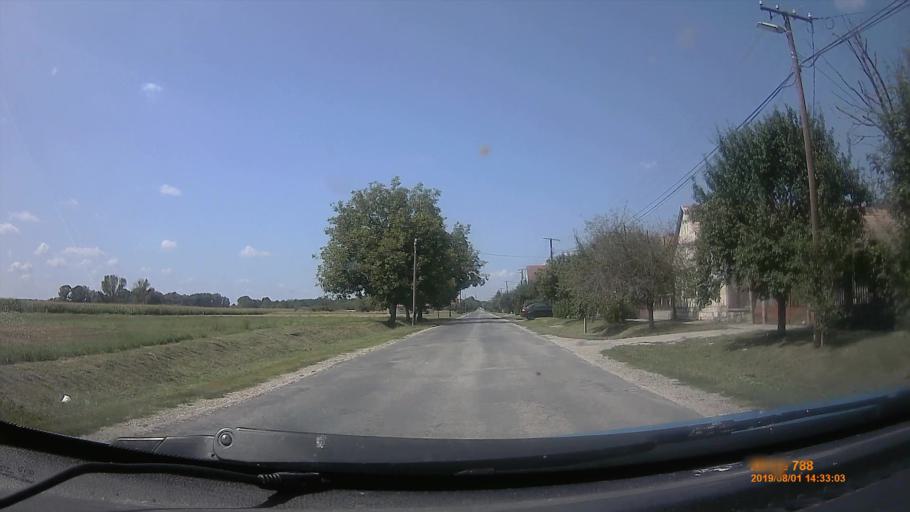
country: HR
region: Osjecko-Baranjska
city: Viljevo
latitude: 45.8172
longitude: 18.1077
